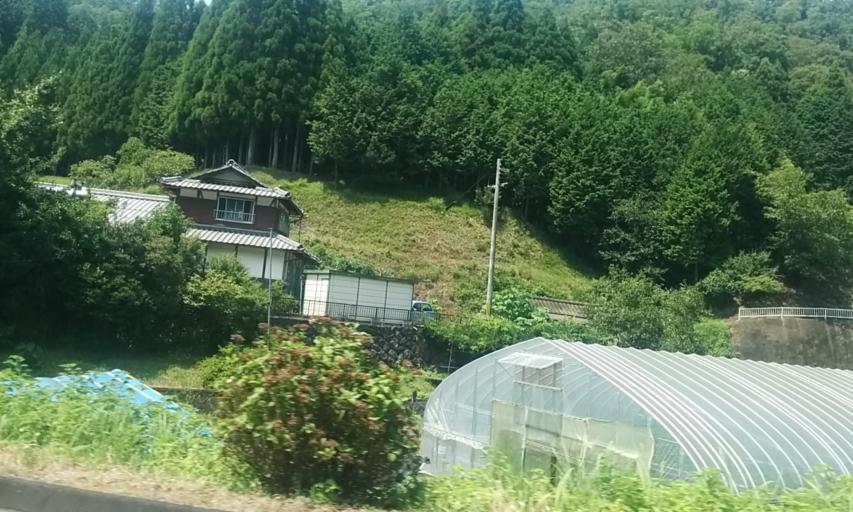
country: JP
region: Kyoto
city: Ayabe
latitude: 35.2143
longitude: 135.2085
